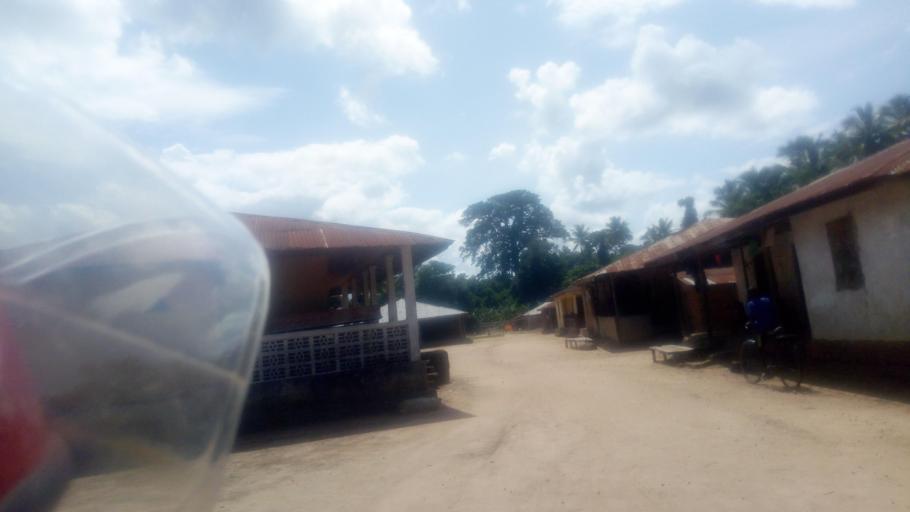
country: SL
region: Northern Province
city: Magburaka
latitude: 8.6510
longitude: -12.0687
